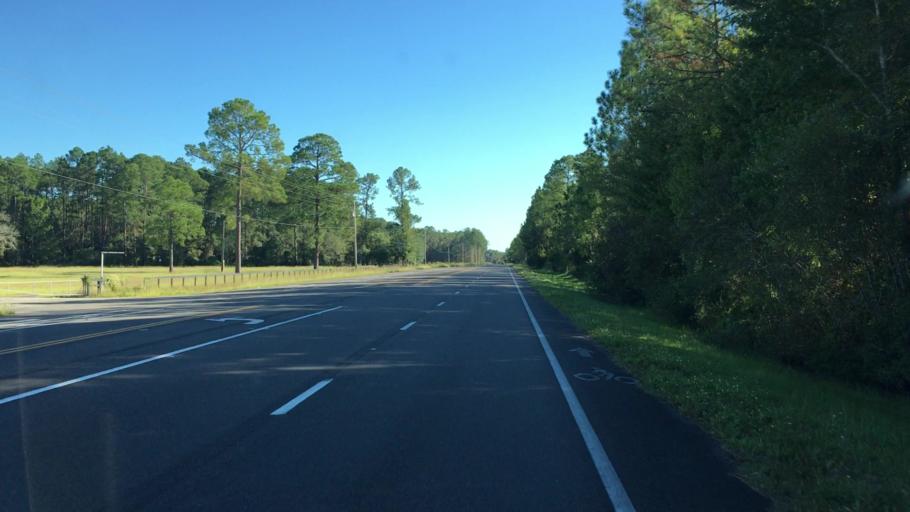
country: US
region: Florida
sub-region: Alachua County
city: Gainesville
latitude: 29.7550
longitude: -82.2784
